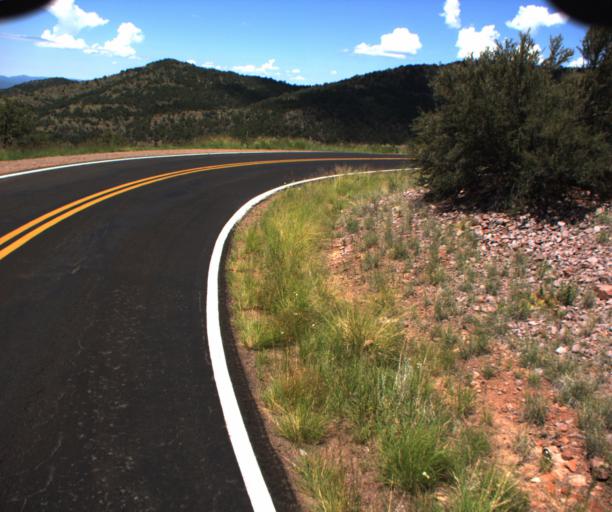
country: US
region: Arizona
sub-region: Greenlee County
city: Morenci
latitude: 33.4005
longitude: -109.3470
